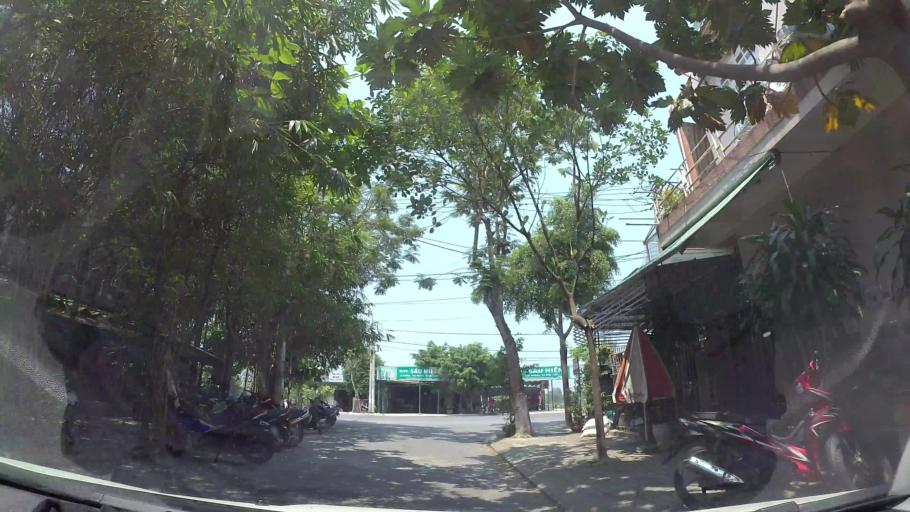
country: VN
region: Da Nang
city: Ngu Hanh Son
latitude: 15.9943
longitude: 108.2554
